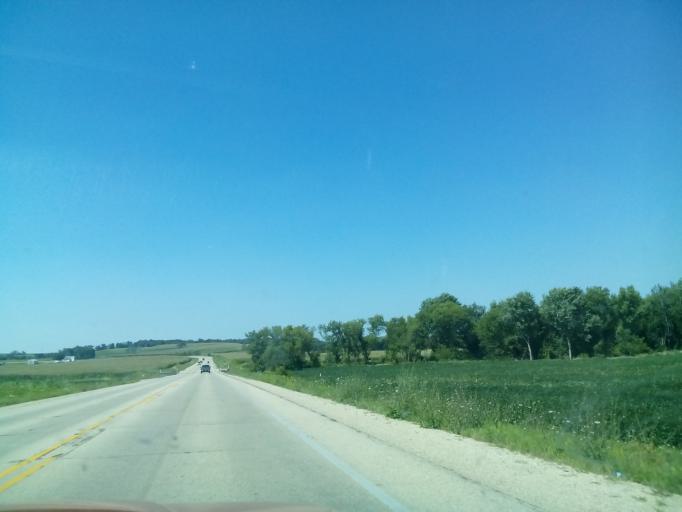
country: US
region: Wisconsin
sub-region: Green County
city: Monticello
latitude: 42.7113
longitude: -89.6062
